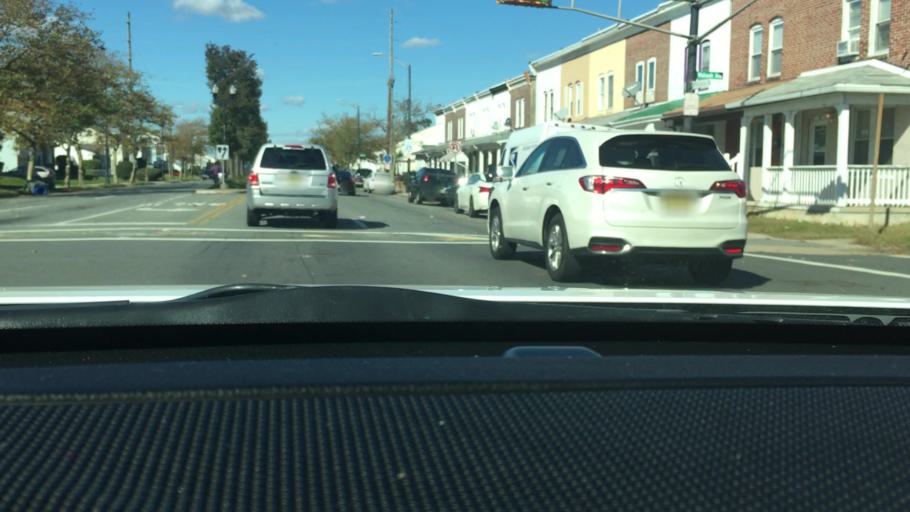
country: US
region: New Jersey
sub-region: Atlantic County
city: Atlantic City
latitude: 39.3666
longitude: -74.4359
